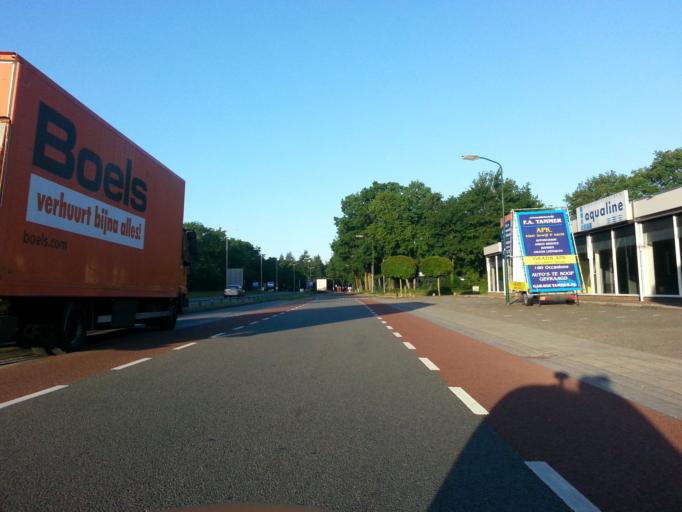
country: NL
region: Utrecht
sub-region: Gemeente Soest
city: Soest
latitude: 52.1216
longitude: 5.2798
